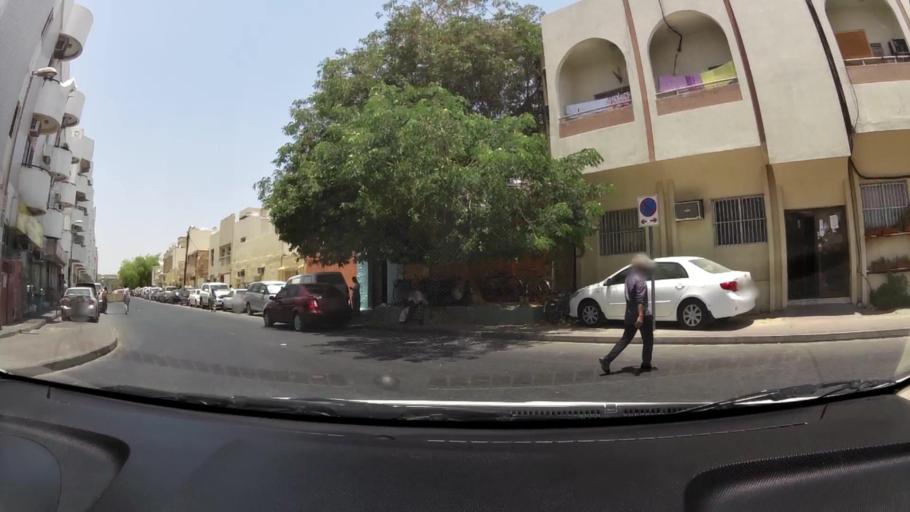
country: AE
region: Ash Shariqah
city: Sharjah
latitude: 25.2780
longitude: 55.3394
